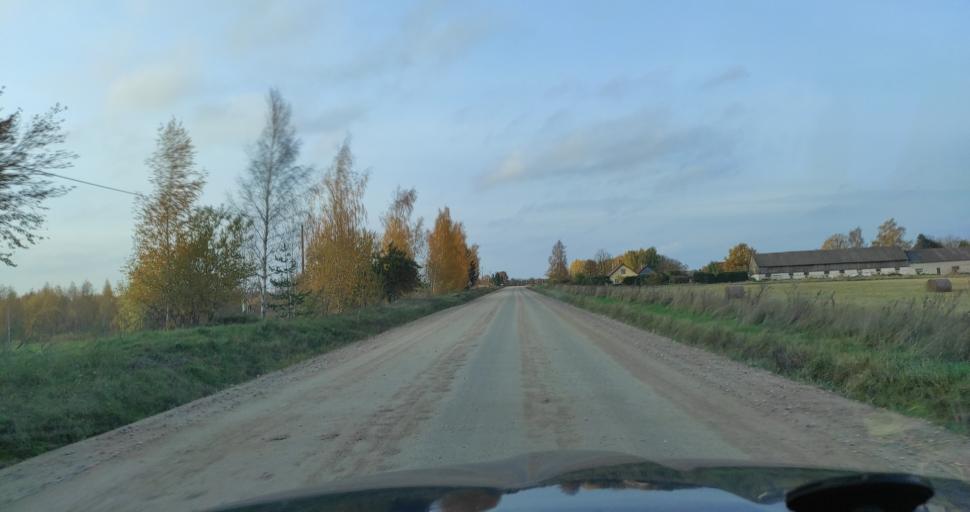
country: LV
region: Vainode
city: Vainode
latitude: 56.4383
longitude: 21.8772
